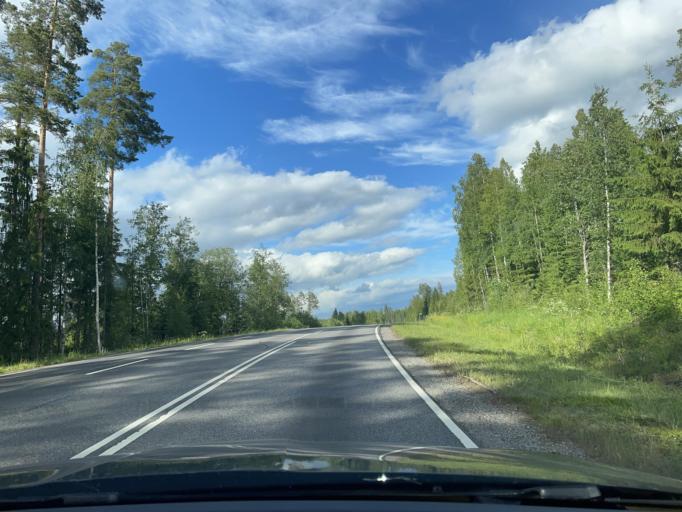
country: FI
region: Central Finland
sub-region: Jyvaeskylae
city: Petaejaevesi
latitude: 62.0905
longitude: 25.1511
